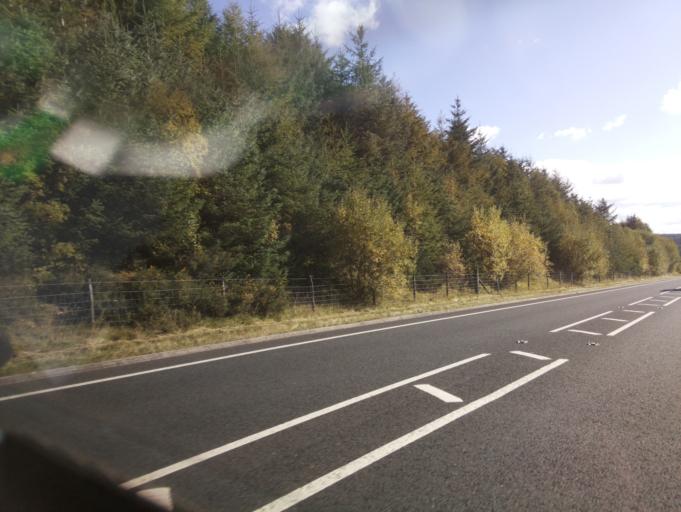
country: GB
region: Wales
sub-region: Rhondda Cynon Taf
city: Hirwaun
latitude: 51.8417
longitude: -3.4641
